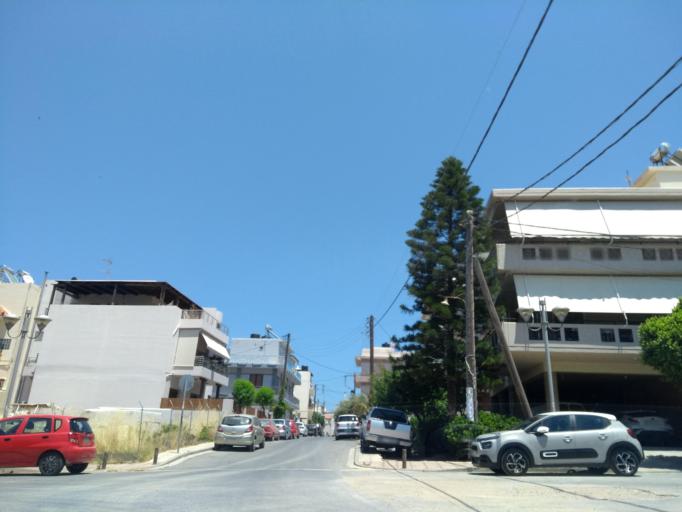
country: GR
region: Crete
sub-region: Nomos Irakleiou
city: Nea Alikarnassos
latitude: 35.3342
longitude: 25.1597
